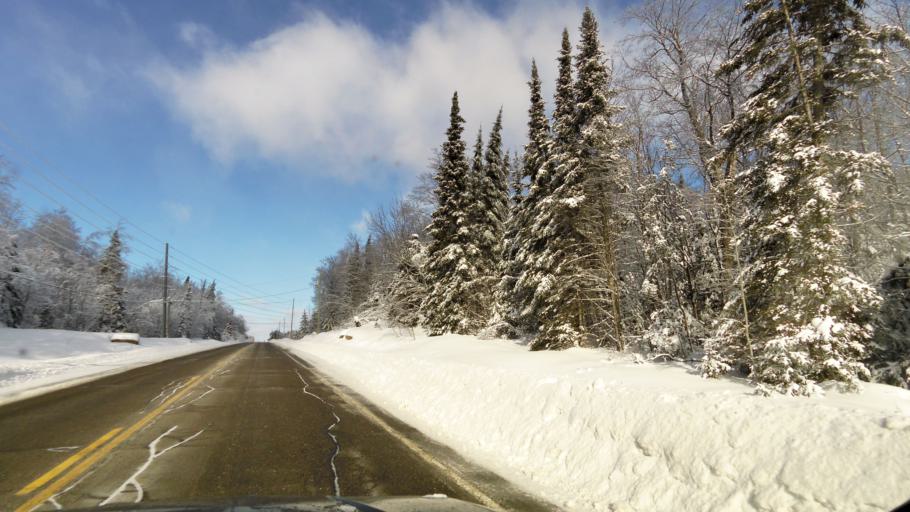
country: CA
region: Ontario
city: Bancroft
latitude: 44.9962
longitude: -78.3002
